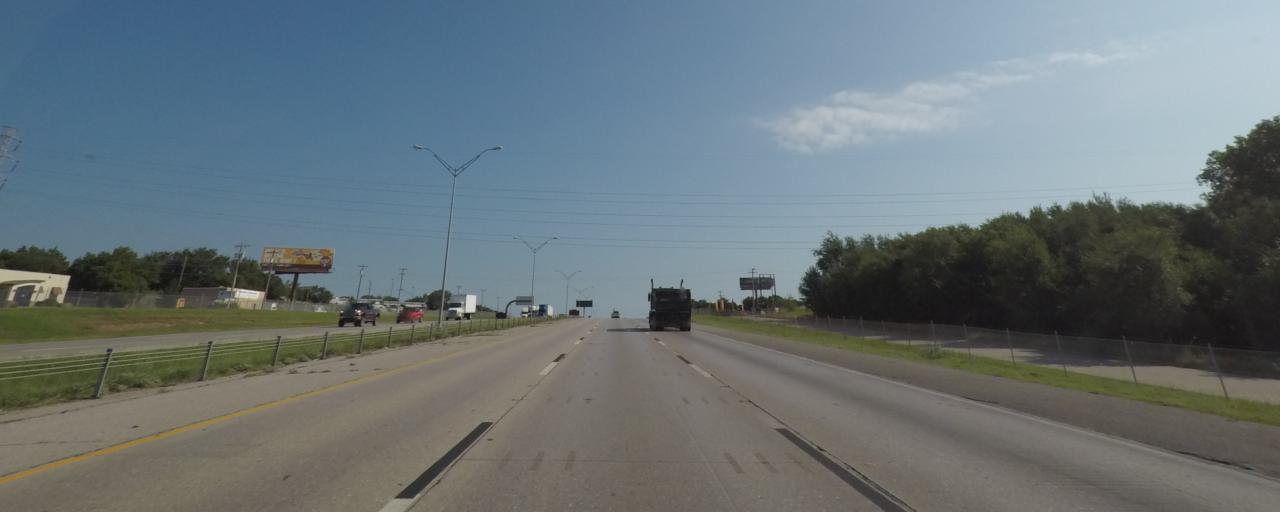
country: US
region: Oklahoma
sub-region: Oklahoma County
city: Spencer
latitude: 35.5692
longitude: -97.4489
